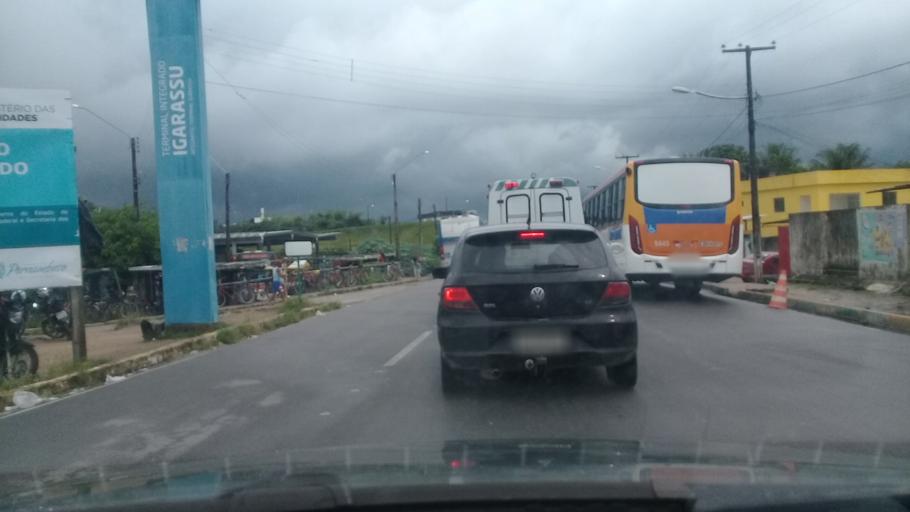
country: BR
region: Pernambuco
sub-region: Igarassu
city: Igarassu
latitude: -7.8320
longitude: -34.9118
